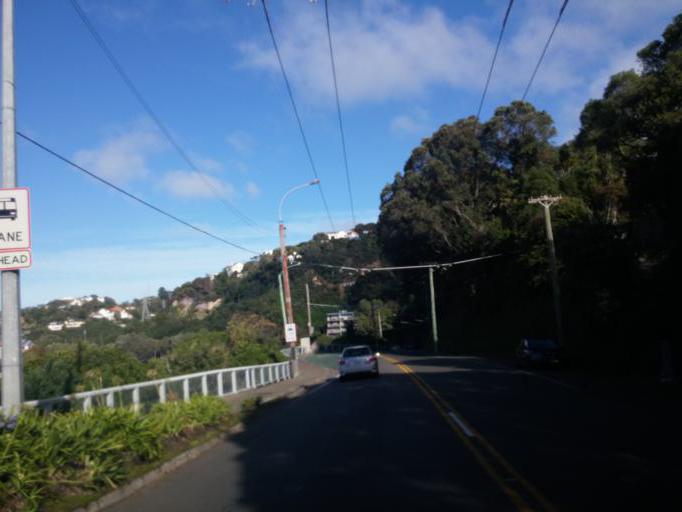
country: NZ
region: Wellington
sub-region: Wellington City
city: Kelburn
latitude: -41.2818
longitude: 174.7524
